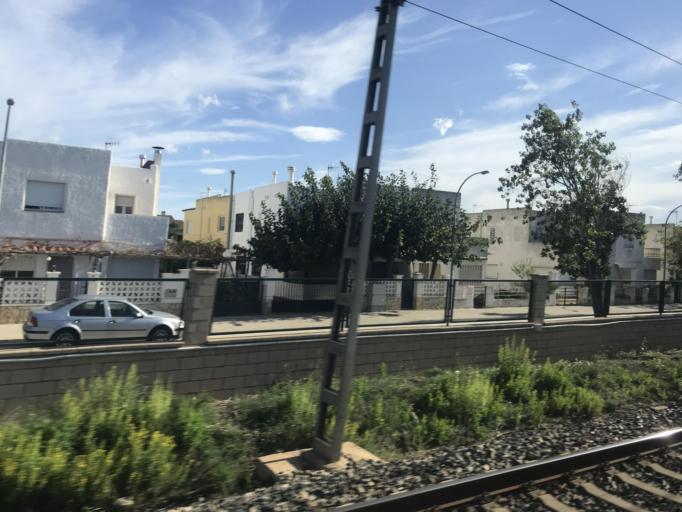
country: ES
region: Catalonia
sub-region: Provincia de Tarragona
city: L'Ampolla
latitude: 40.8168
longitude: 0.7164
